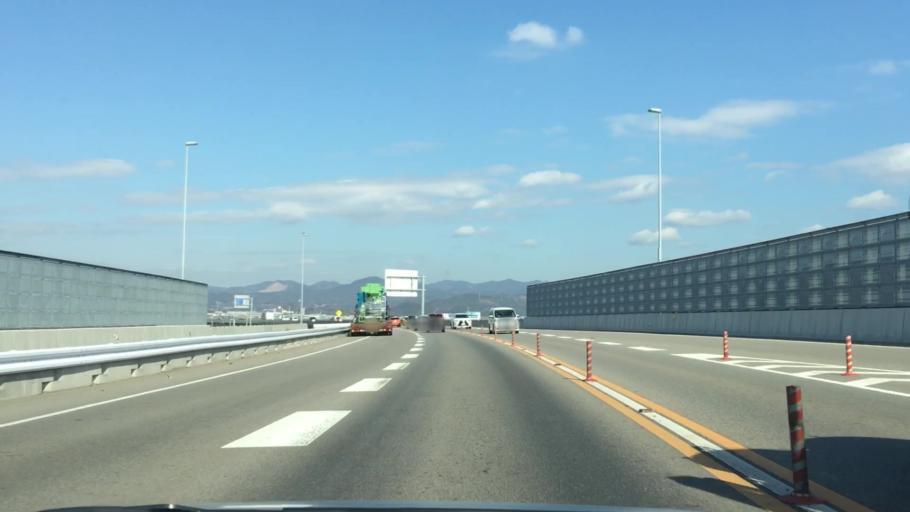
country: JP
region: Aichi
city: Kozakai-cho
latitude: 34.8042
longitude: 137.3373
